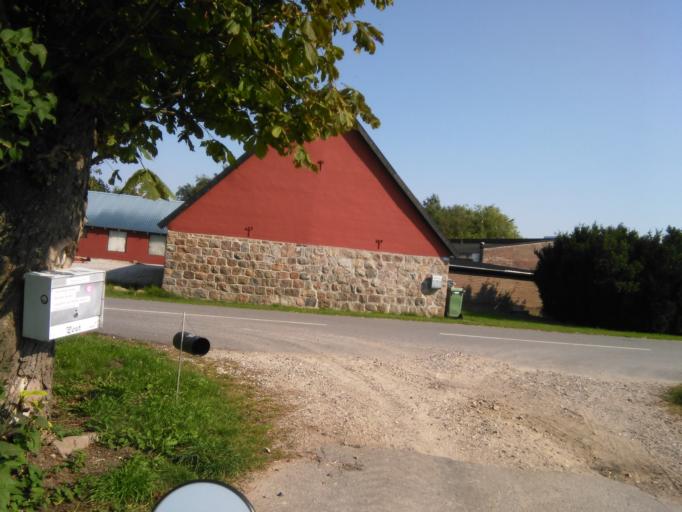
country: DK
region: Central Jutland
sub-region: Arhus Kommune
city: Framlev
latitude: 56.1297
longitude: 9.9898
